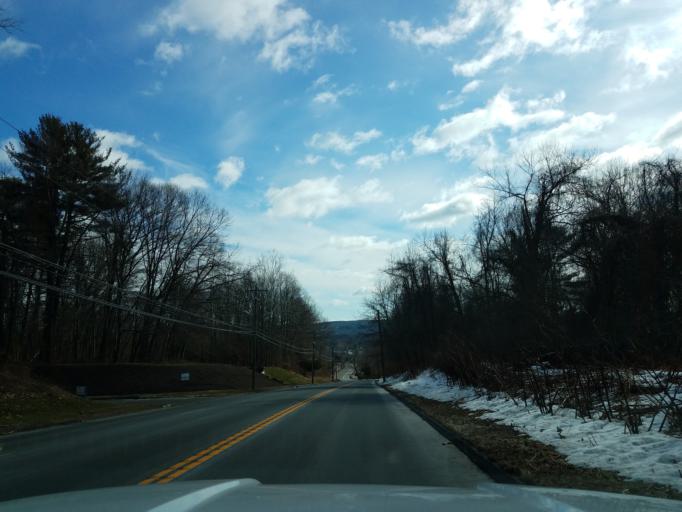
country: US
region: Connecticut
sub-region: Hartford County
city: Plainville
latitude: 41.6397
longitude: -72.8880
